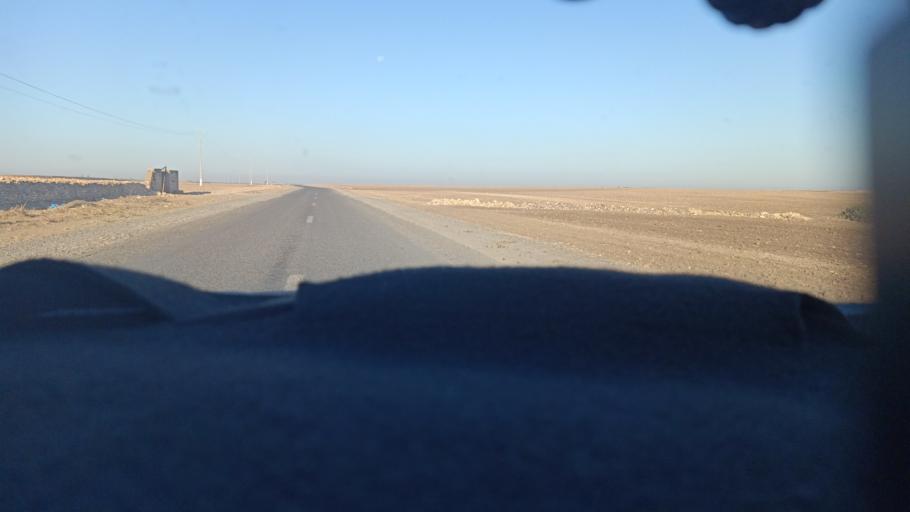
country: MA
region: Doukkala-Abda
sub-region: Safi
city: Youssoufia
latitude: 32.3711
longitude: -8.6827
